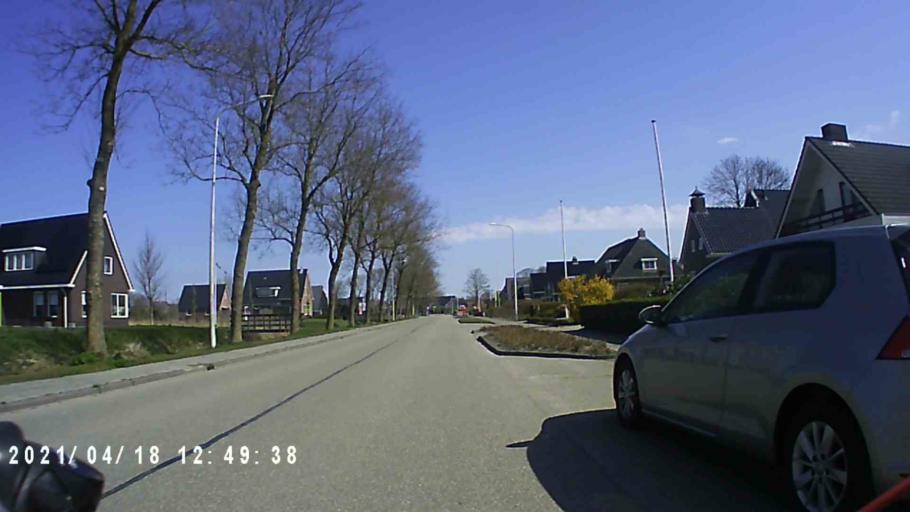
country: NL
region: Friesland
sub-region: Gemeente Dongeradeel
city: Anjum
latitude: 53.3758
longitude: 6.0534
